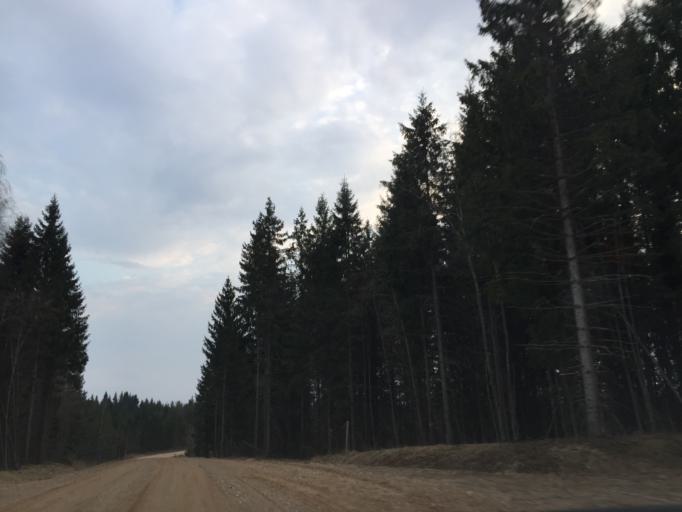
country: LV
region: Raunas
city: Rauna
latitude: 57.1146
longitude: 25.5914
